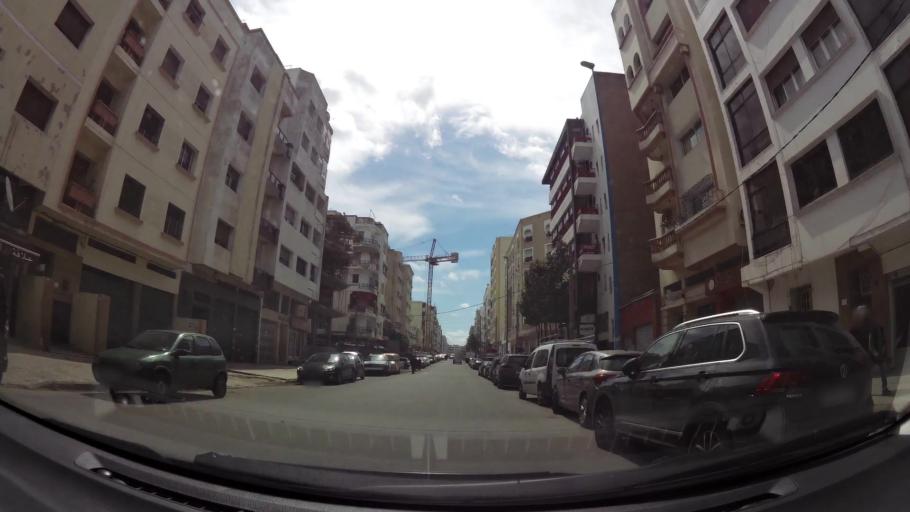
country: MA
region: Grand Casablanca
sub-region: Casablanca
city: Casablanca
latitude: 33.5816
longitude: -7.6424
